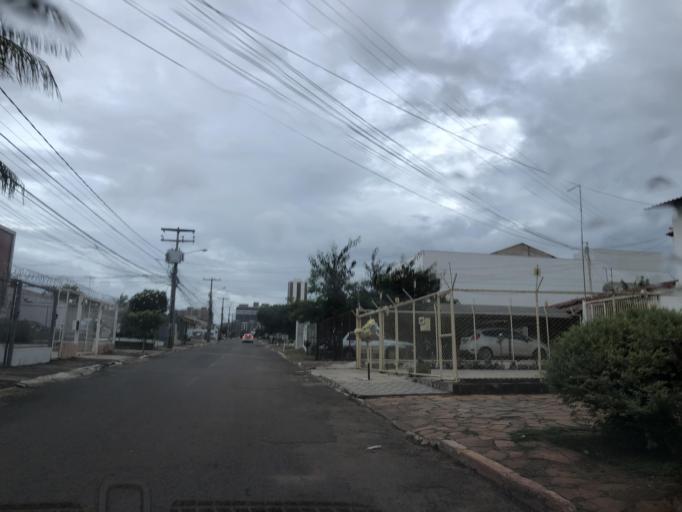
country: BR
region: Federal District
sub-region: Brasilia
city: Brasilia
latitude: -15.8405
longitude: -48.0613
